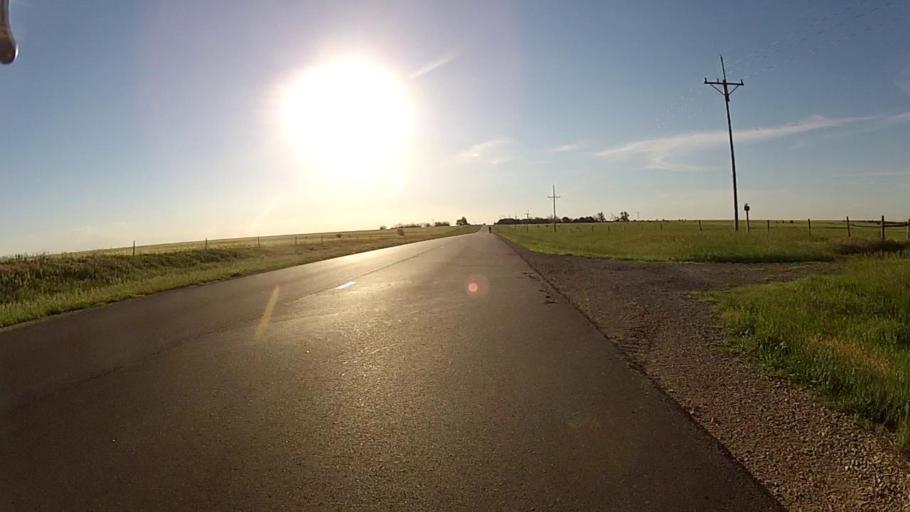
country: US
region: Kansas
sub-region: Comanche County
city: Coldwater
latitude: 37.2817
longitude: -99.1566
